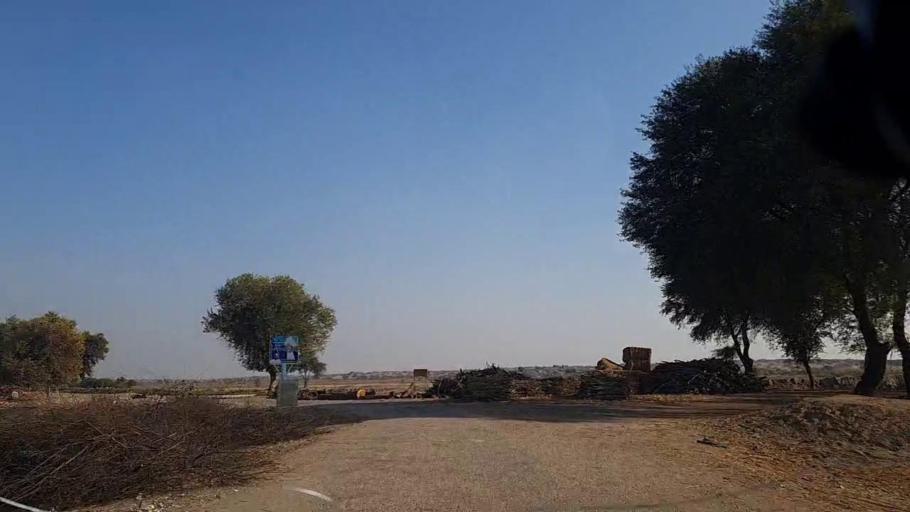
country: PK
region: Sindh
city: Khanpur
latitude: 27.6426
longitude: 69.6011
